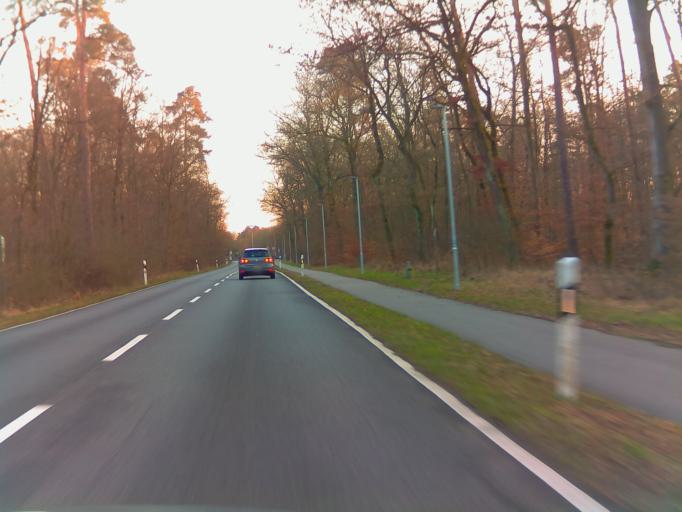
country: DE
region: Baden-Wuerttemberg
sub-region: Karlsruhe Region
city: Walldorf
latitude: 49.3186
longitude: 8.6443
